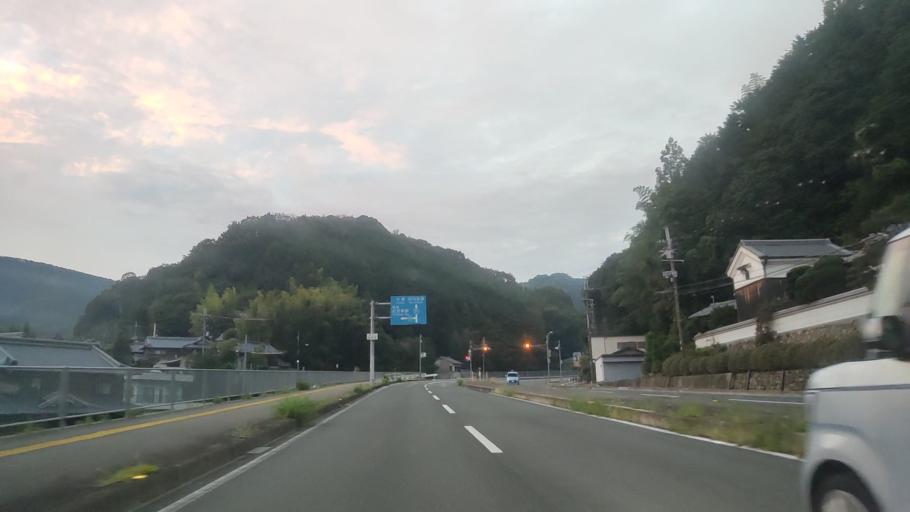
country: JP
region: Wakayama
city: Hashimoto
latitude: 34.3619
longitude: 135.6061
